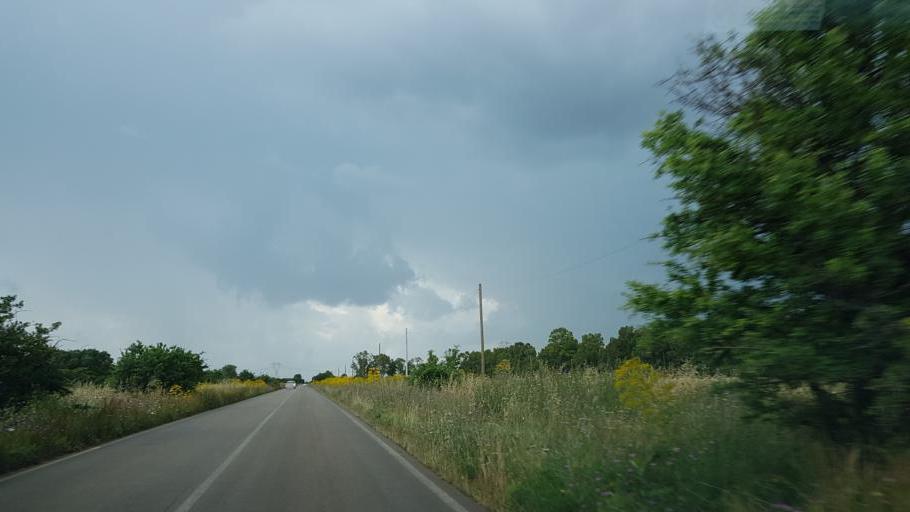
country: IT
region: Apulia
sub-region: Provincia di Brindisi
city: San Pancrazio Salentino
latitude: 40.3339
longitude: 17.8512
